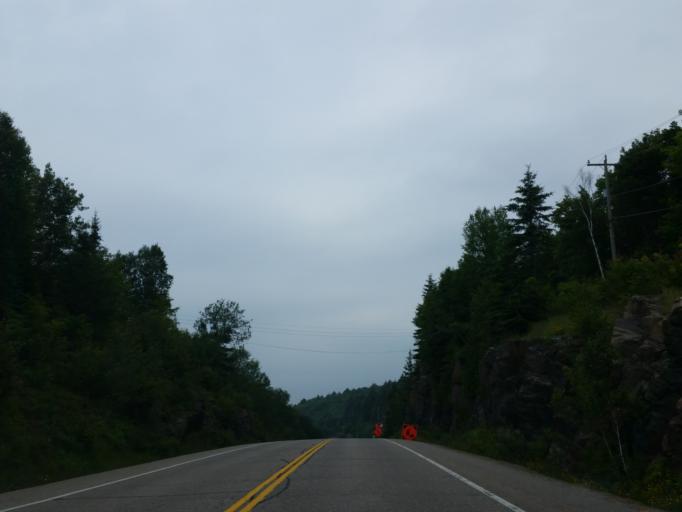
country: CA
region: Ontario
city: Mattawa
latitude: 45.5810
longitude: -78.4616
